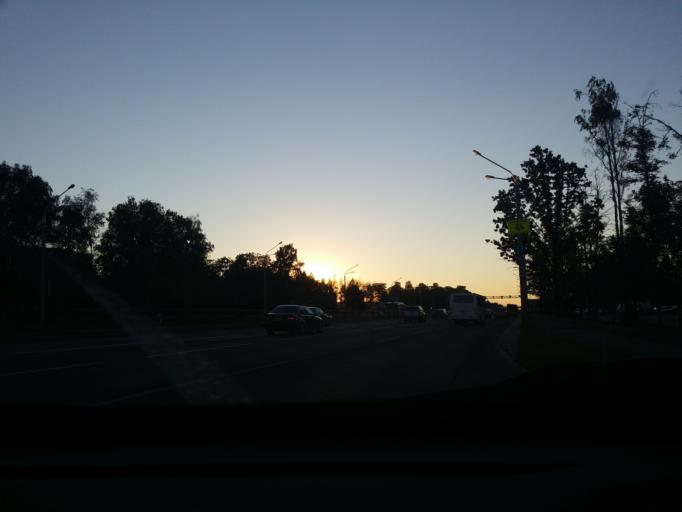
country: BY
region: Minsk
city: Vyaliki Trastsyanets
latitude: 53.8478
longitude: 27.7069
